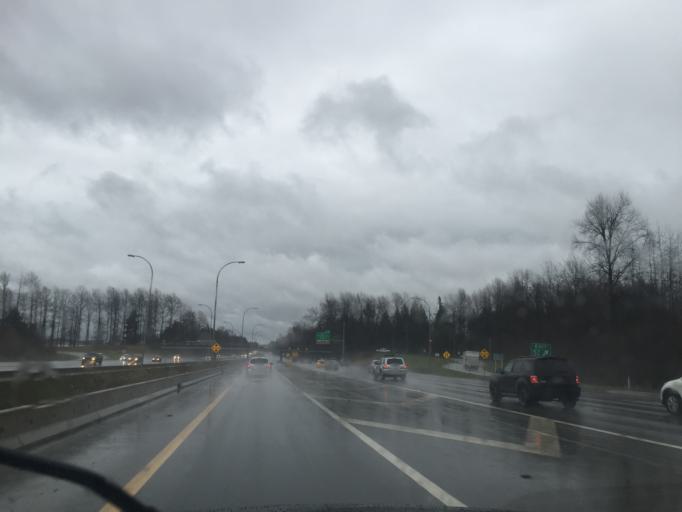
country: CA
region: British Columbia
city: Pitt Meadows
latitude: 49.1713
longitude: -122.6962
